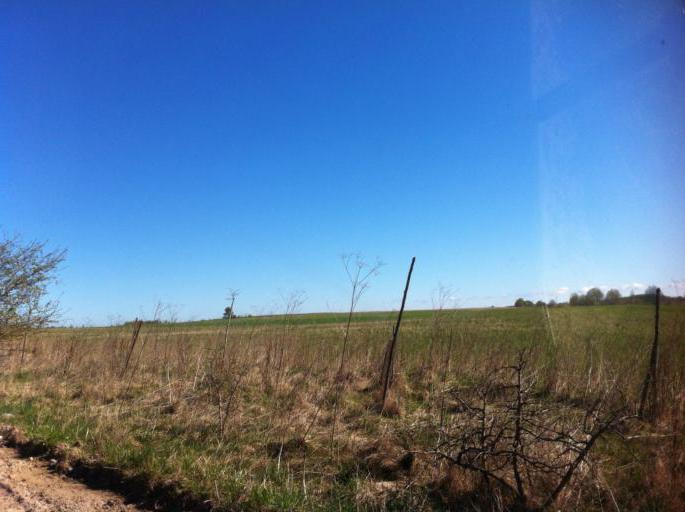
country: RU
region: Pskov
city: Izborsk
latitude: 57.8105
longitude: 27.9797
